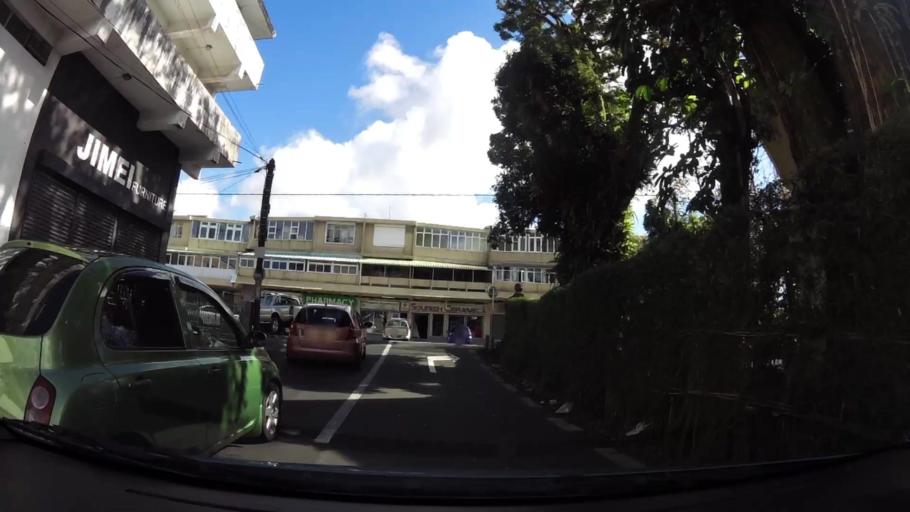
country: MU
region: Plaines Wilhems
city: Curepipe
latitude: -20.3238
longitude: 57.5277
